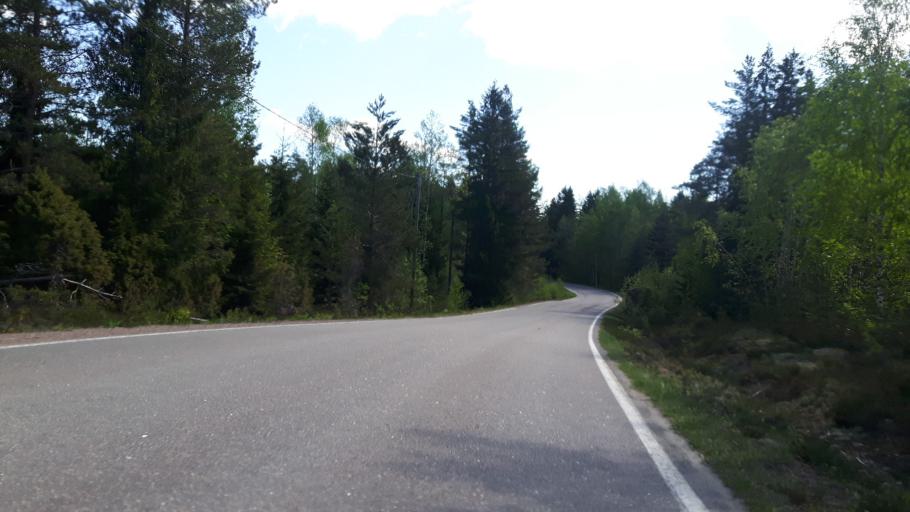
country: FI
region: Kymenlaakso
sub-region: Kotka-Hamina
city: Hamina
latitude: 60.5140
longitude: 27.4106
